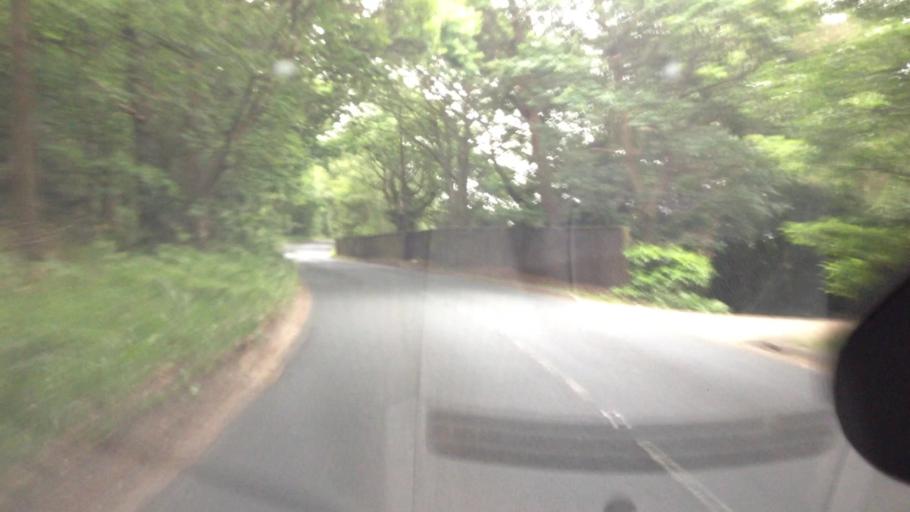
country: GB
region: England
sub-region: City and Borough of Wakefield
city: Woolley
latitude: 53.6175
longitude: -1.5390
